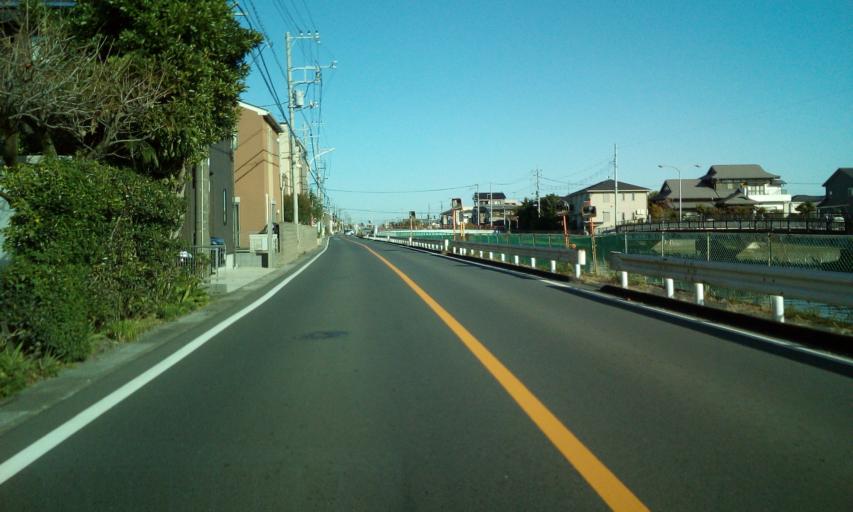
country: JP
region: Chiba
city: Matsudo
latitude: 35.8044
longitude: 139.8840
